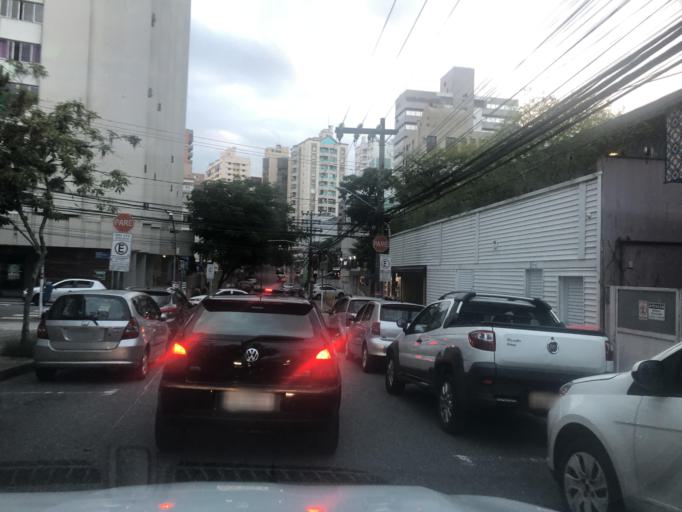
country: BR
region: Santa Catarina
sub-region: Florianopolis
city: Florianopolis
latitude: -27.5929
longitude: -48.5509
